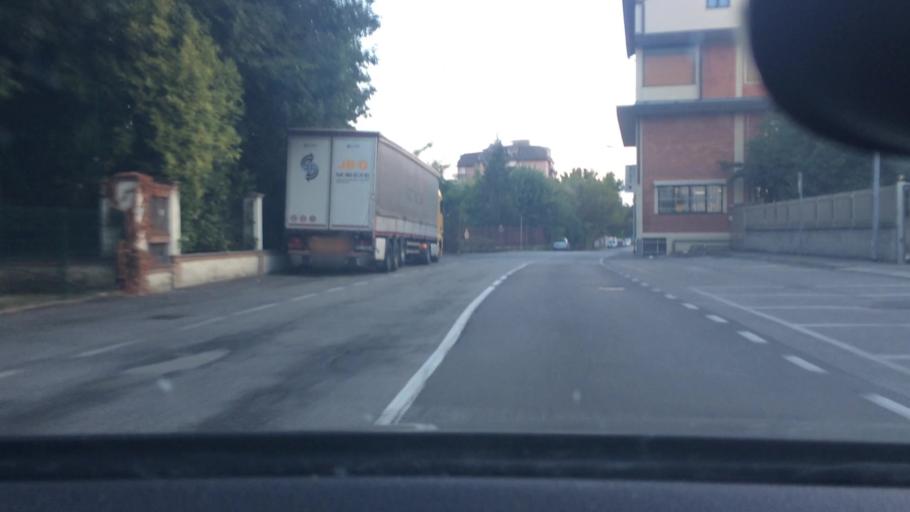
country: IT
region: Lombardy
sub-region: Citta metropolitana di Milano
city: Pogliano Milanese
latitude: 45.5432
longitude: 9.0007
